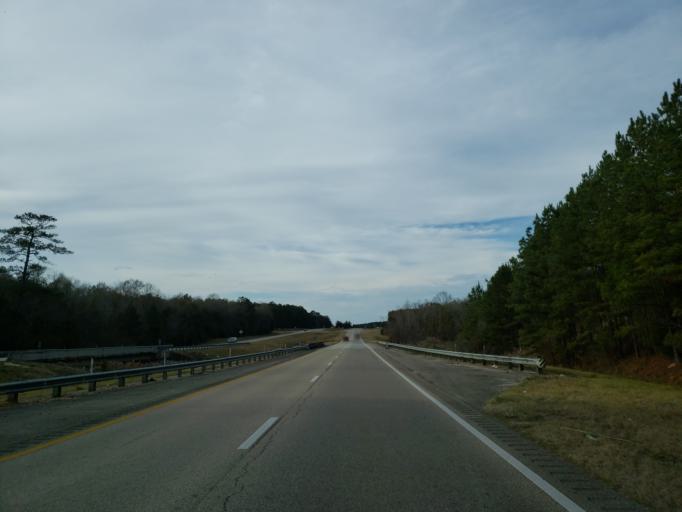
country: US
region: Mississippi
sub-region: Wayne County
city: Waynesboro
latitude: 31.6237
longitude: -88.5843
